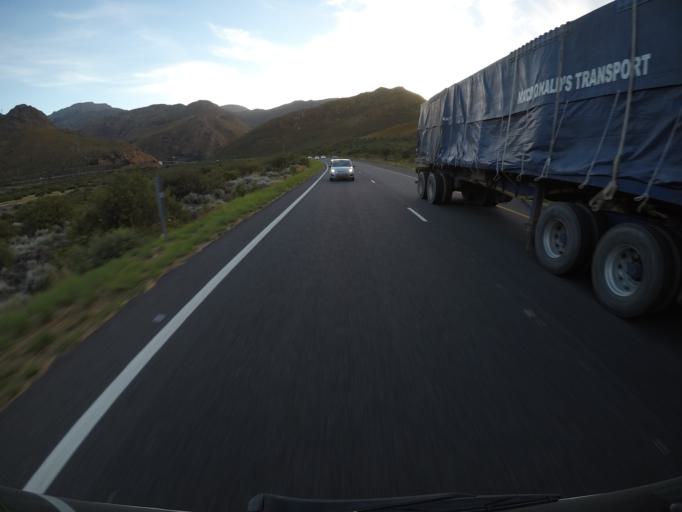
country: ZA
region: Western Cape
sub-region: Cape Winelands District Municipality
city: Paarl
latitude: -33.7268
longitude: 19.1236
